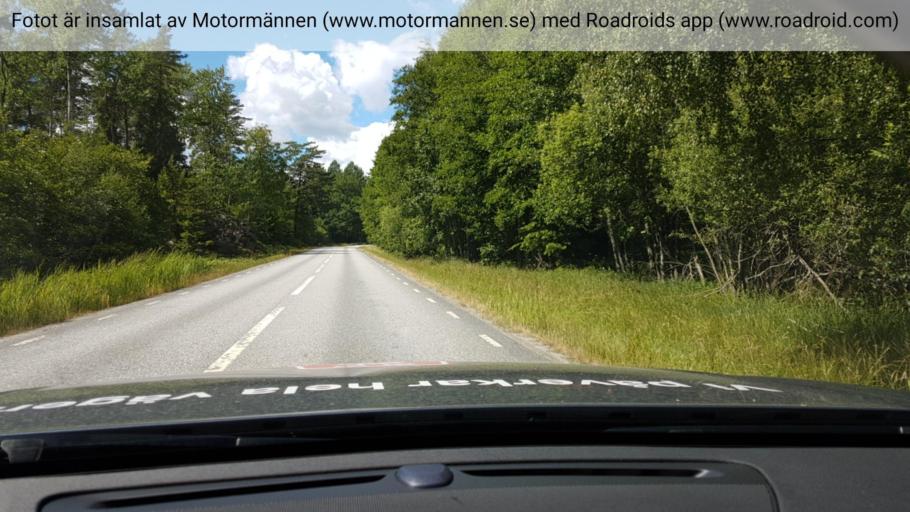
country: SE
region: Stockholm
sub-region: Varmdo Kommun
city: Hemmesta
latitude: 59.3910
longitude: 18.4998
